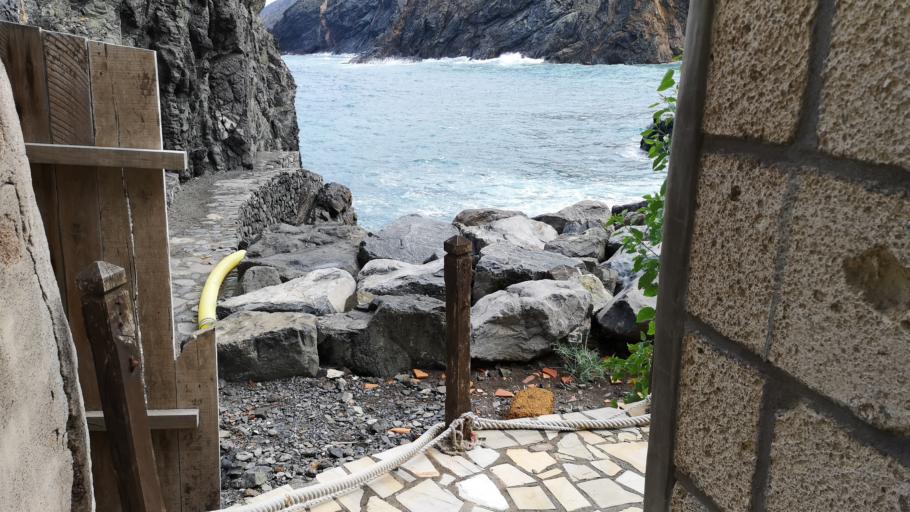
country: ES
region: Canary Islands
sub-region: Provincia de Santa Cruz de Tenerife
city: Vallehermosa
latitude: 28.2055
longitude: -17.2534
